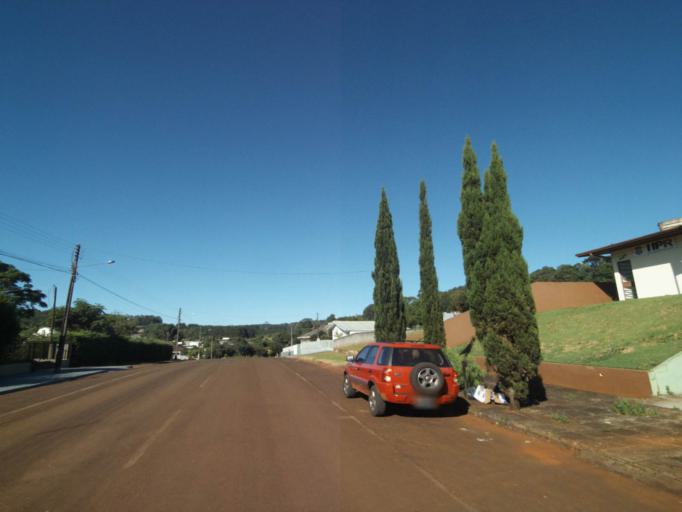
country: BR
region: Parana
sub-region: Pato Branco
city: Pato Branco
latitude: -26.2635
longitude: -52.7820
